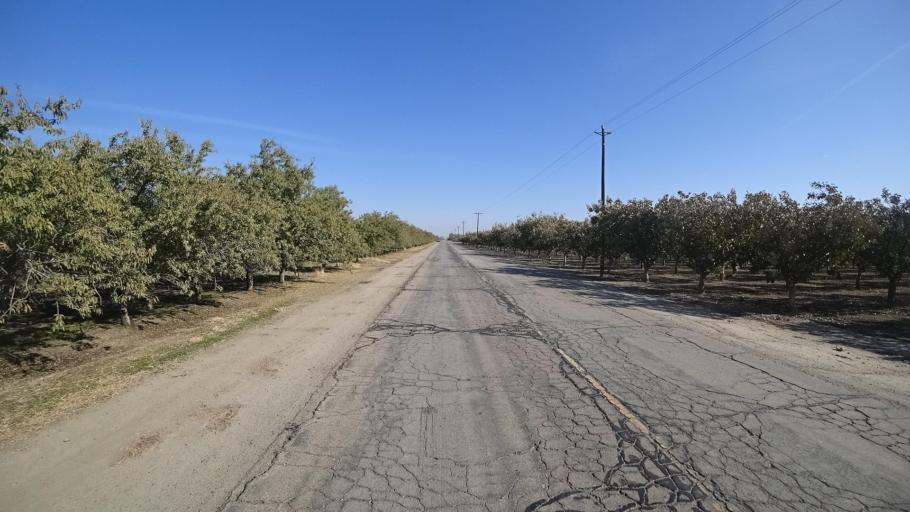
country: US
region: California
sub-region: Kern County
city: Wasco
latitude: 35.6669
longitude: -119.3514
